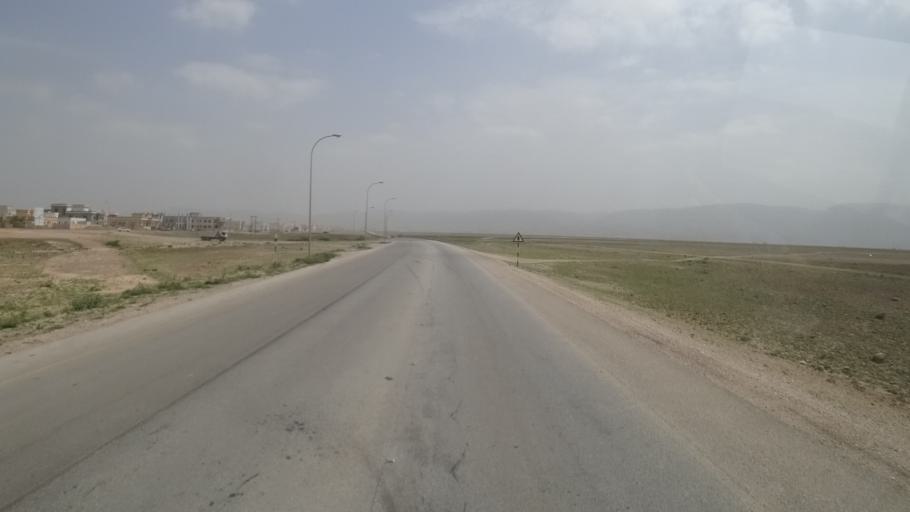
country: OM
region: Zufar
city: Salalah
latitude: 17.0671
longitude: 54.2171
